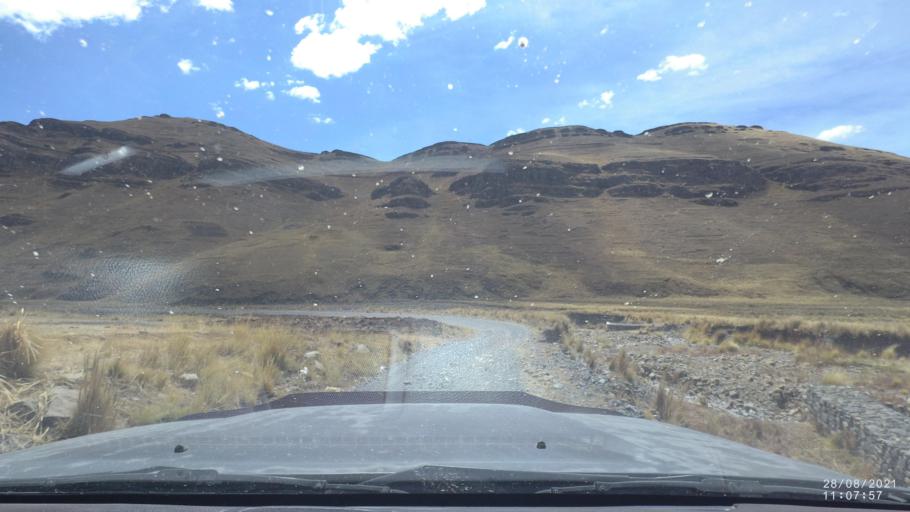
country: BO
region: Cochabamba
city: Cochabamba
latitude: -17.1685
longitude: -66.3007
